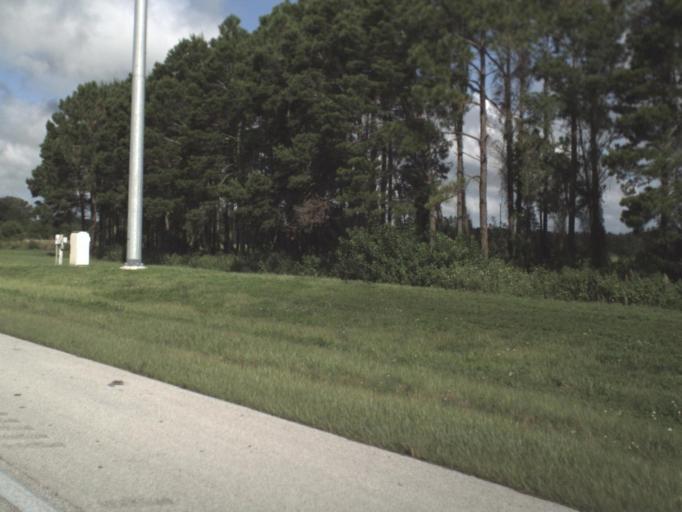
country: US
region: Florida
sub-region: Polk County
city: Polk City
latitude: 28.1576
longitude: -81.8317
